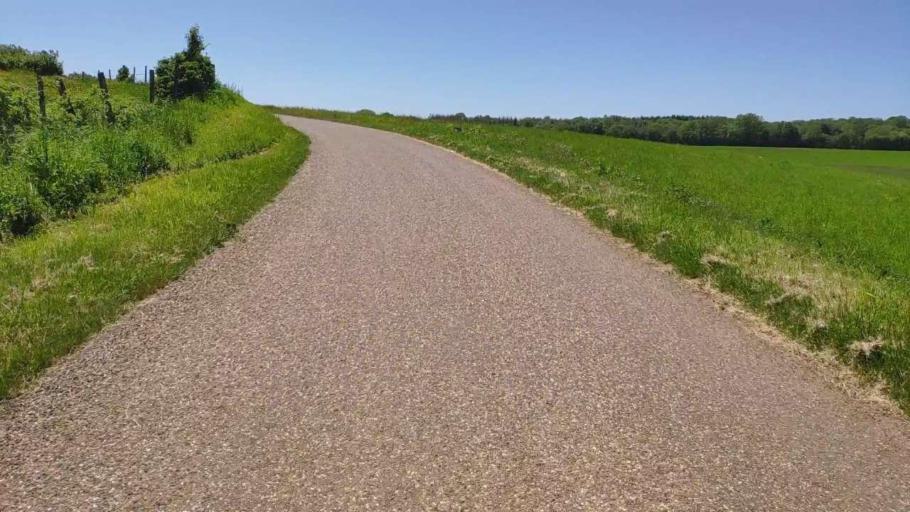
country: FR
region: Franche-Comte
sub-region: Departement du Jura
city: Poligny
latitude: 46.7360
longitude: 5.6889
